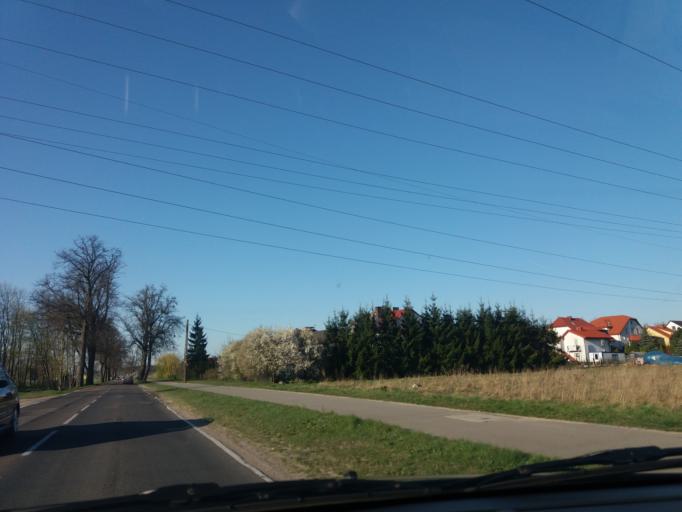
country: PL
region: Warmian-Masurian Voivodeship
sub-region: Powiat nidzicki
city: Nidzica
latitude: 53.3757
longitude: 20.4302
